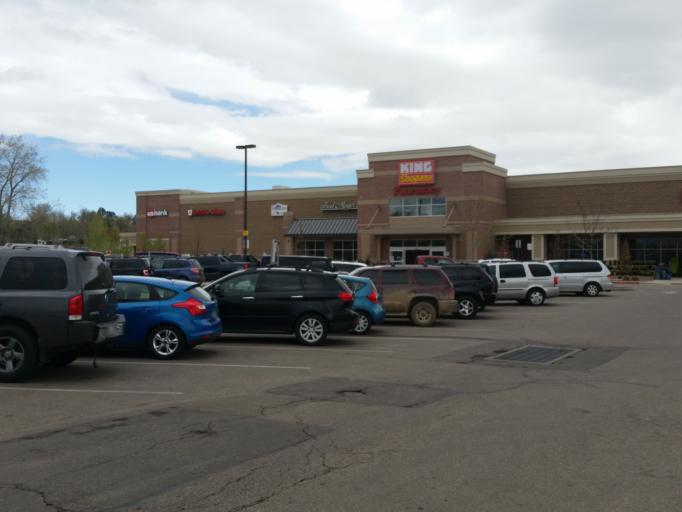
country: US
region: Colorado
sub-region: Larimer County
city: Fort Collins
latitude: 40.6118
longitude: -105.0745
